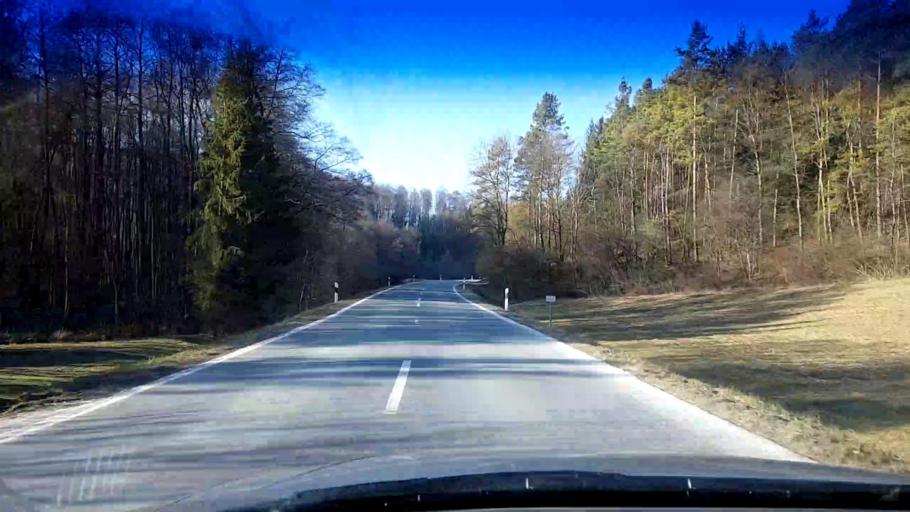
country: DE
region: Bavaria
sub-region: Upper Franconia
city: Aufsess
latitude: 49.8876
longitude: 11.2246
